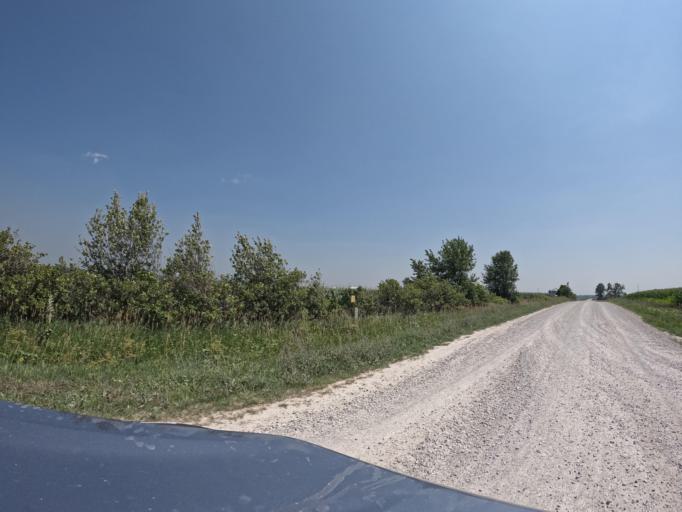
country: US
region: Iowa
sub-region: Keokuk County
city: Sigourney
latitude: 41.3403
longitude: -92.2387
